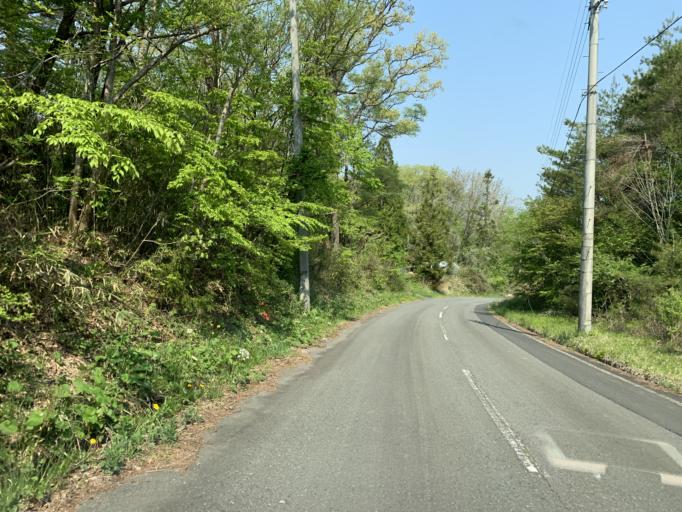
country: JP
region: Iwate
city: Ichinoseki
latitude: 38.8916
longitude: 141.0635
